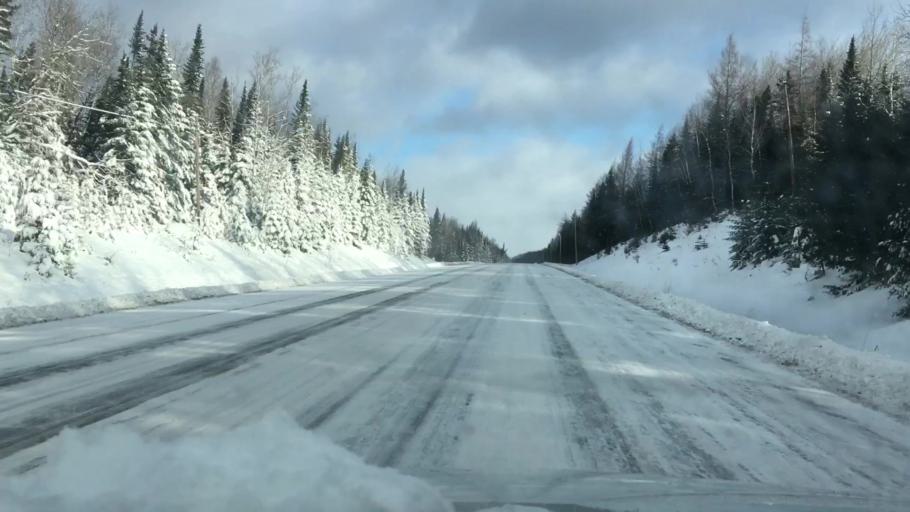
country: US
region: Maine
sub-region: Aroostook County
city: Van Buren
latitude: 47.0254
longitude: -68.0112
